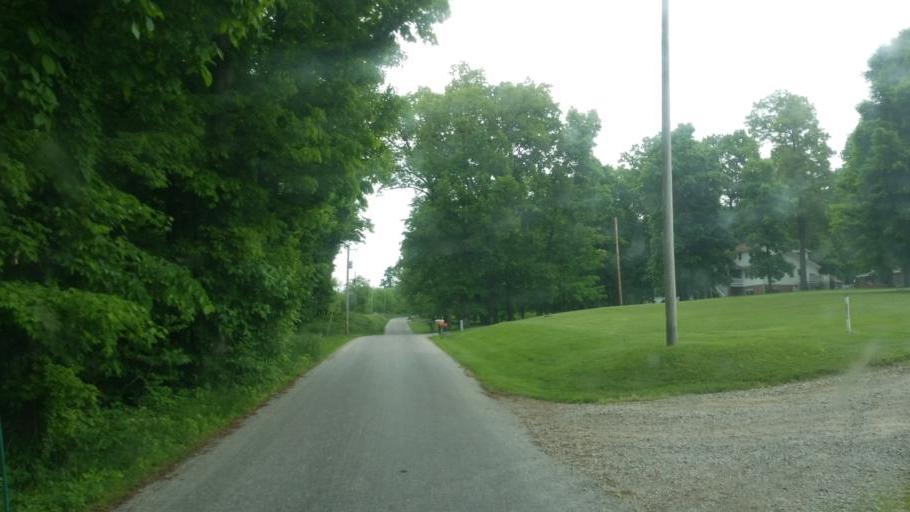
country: US
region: Ohio
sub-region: Stark County
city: Brewster
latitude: 40.6459
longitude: -81.7319
